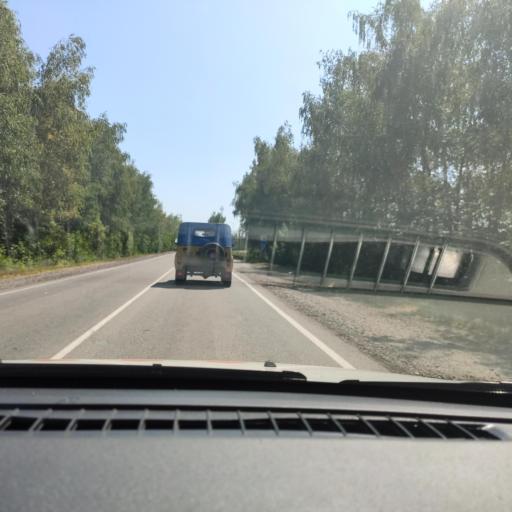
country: RU
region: Voronezj
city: Imeni Pervogo Maya
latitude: 50.7275
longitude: 39.3995
